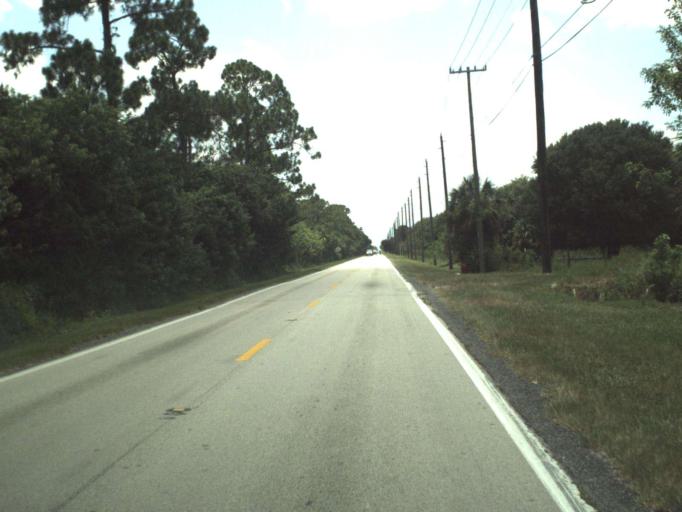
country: US
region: Florida
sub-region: Saint Lucie County
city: Fort Pierce South
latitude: 27.3744
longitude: -80.4235
